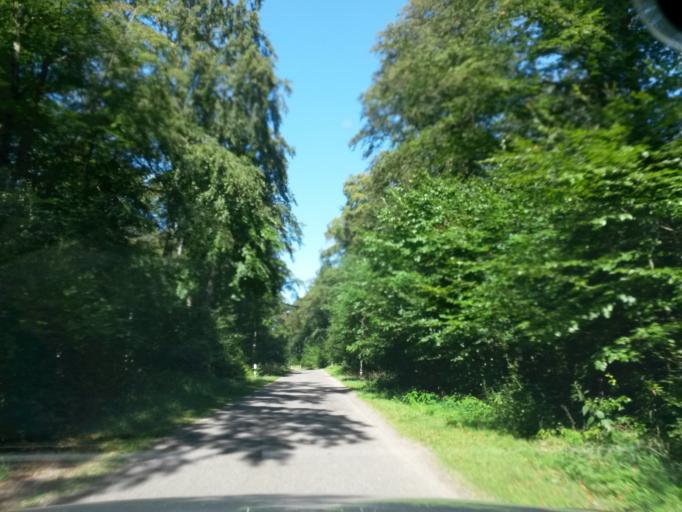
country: DE
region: Brandenburg
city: Templin
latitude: 53.2393
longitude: 13.4531
